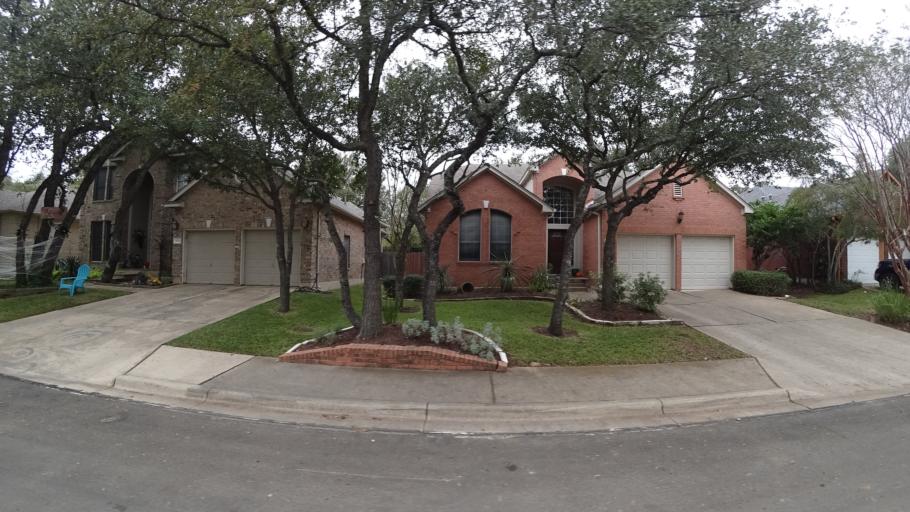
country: US
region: Texas
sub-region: Travis County
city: Shady Hollow
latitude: 30.2130
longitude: -97.8848
